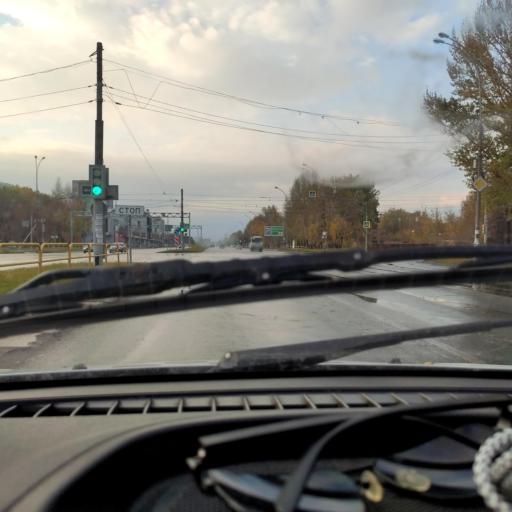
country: RU
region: Samara
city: Tol'yatti
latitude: 53.5381
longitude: 49.2837
